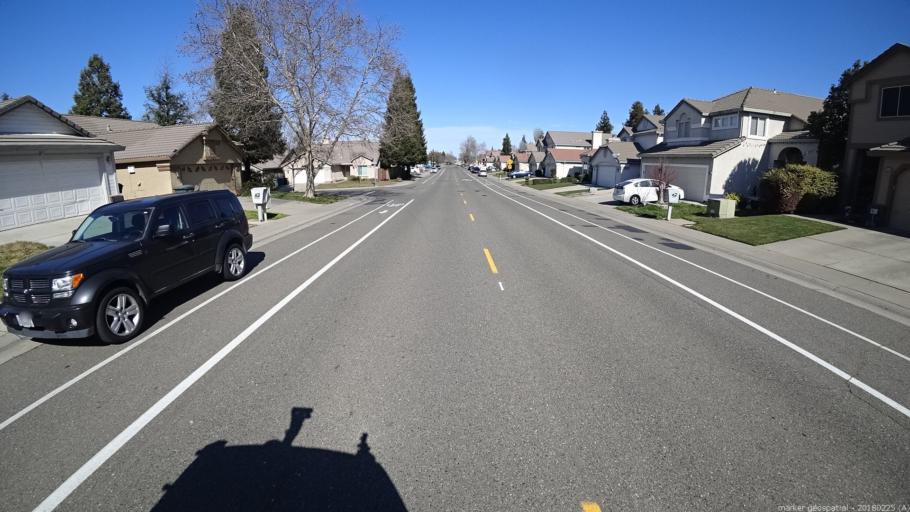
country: US
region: California
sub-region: Sacramento County
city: Antelope
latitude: 38.7155
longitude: -121.3397
